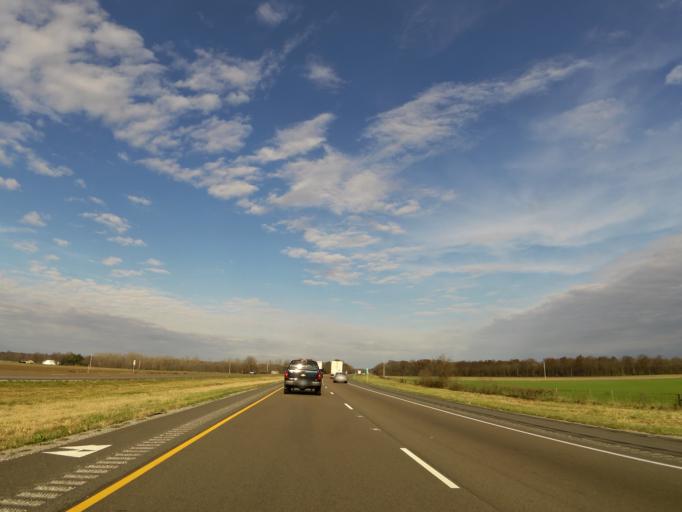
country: US
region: Illinois
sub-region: Washington County
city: Okawville
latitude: 38.4605
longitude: -89.5670
